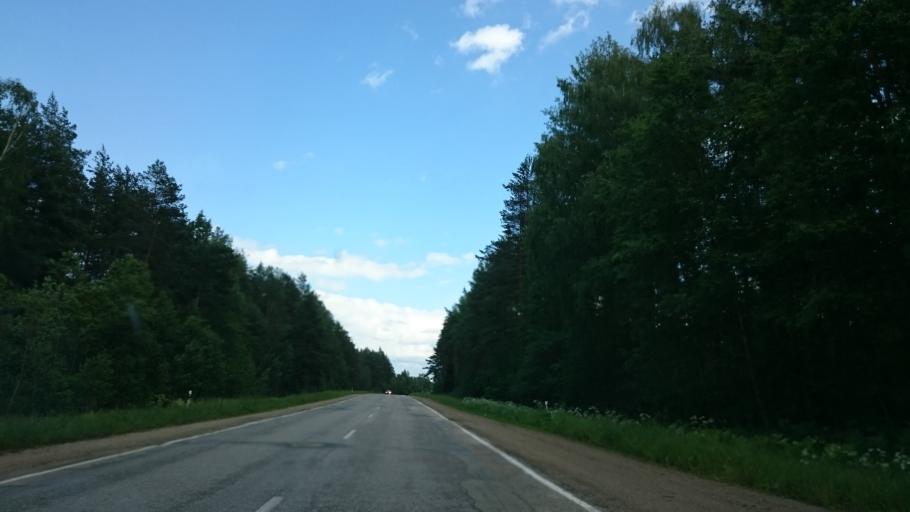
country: LV
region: Ludzas Rajons
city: Ludza
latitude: 56.5350
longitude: 27.6584
